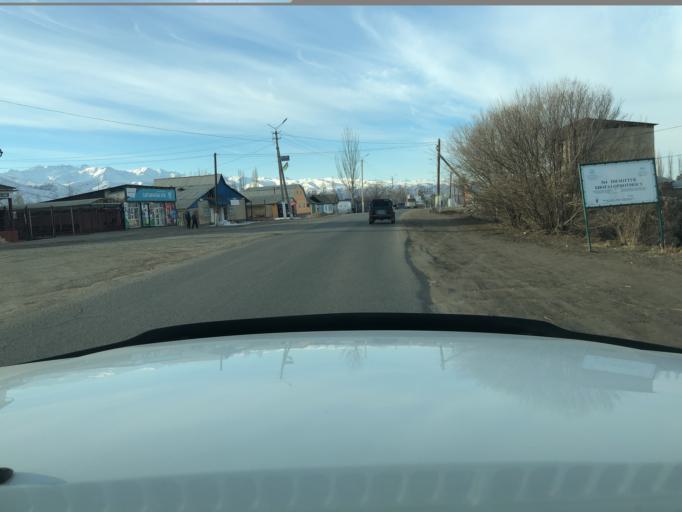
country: KG
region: Ysyk-Koel
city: Pokrovka
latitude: 42.3461
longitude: 78.0131
